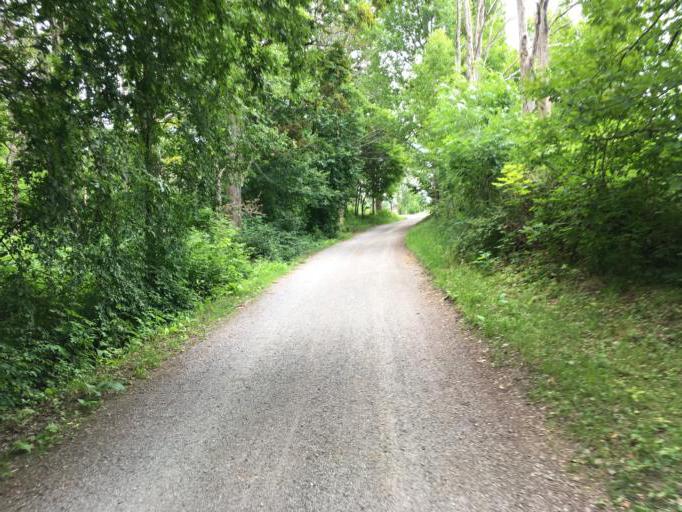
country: SE
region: Uppsala
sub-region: Uppsala Kommun
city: Uppsala
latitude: 59.8431
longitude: 17.6465
